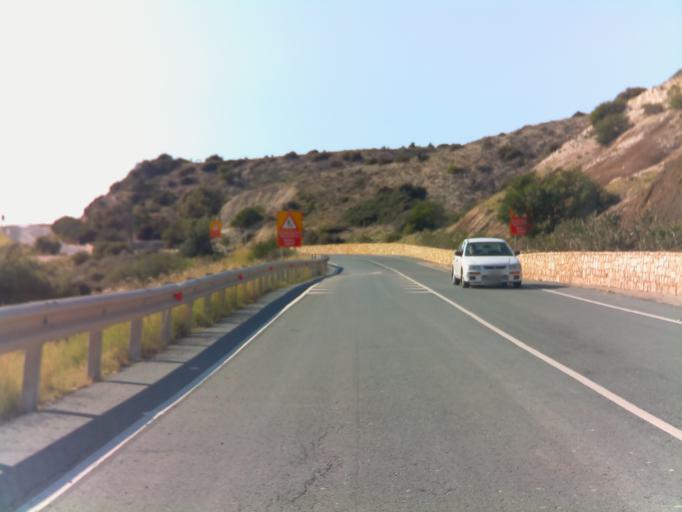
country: CY
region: Limassol
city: Pissouri
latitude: 34.6659
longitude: 32.6303
